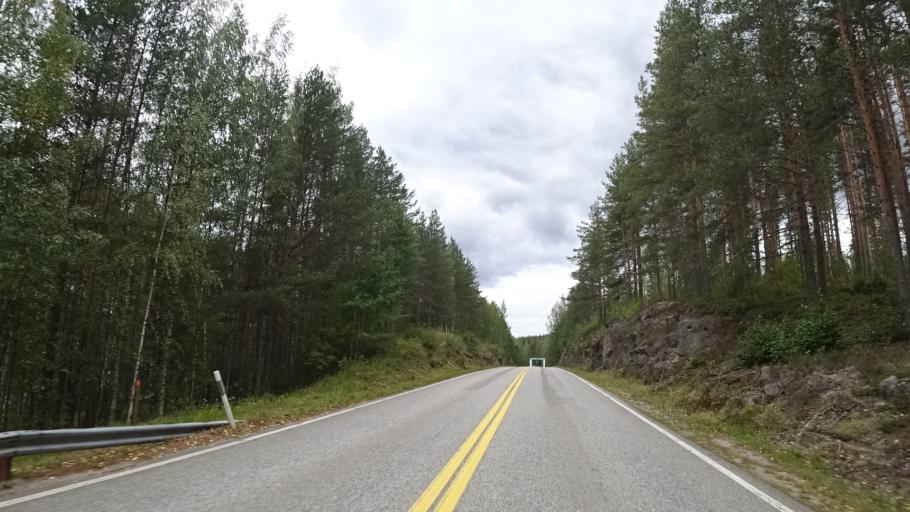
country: FI
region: North Karelia
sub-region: Joensuu
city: Ilomantsi
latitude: 62.6194
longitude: 31.2017
